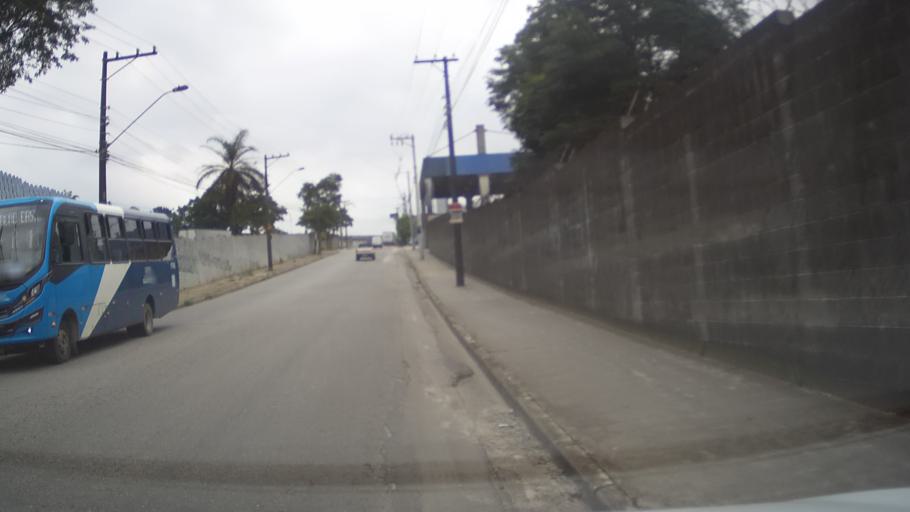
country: BR
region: Sao Paulo
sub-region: Itaquaquecetuba
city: Itaquaquecetuba
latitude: -23.4301
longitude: -46.3944
